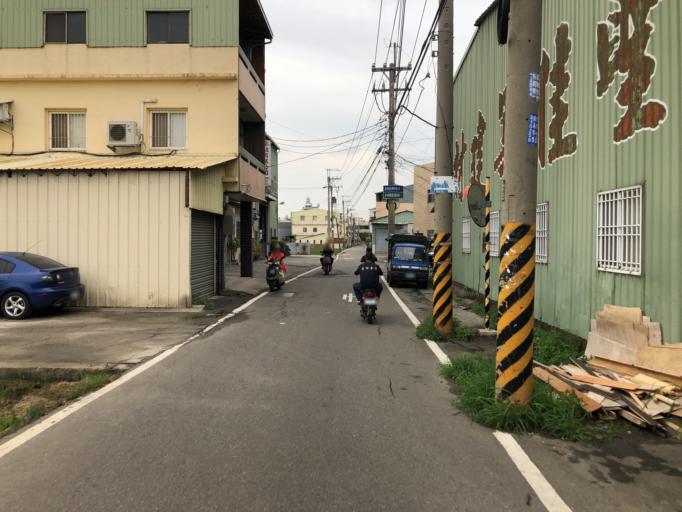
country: TW
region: Taiwan
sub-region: Taichung City
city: Taichung
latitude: 24.0594
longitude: 120.6834
